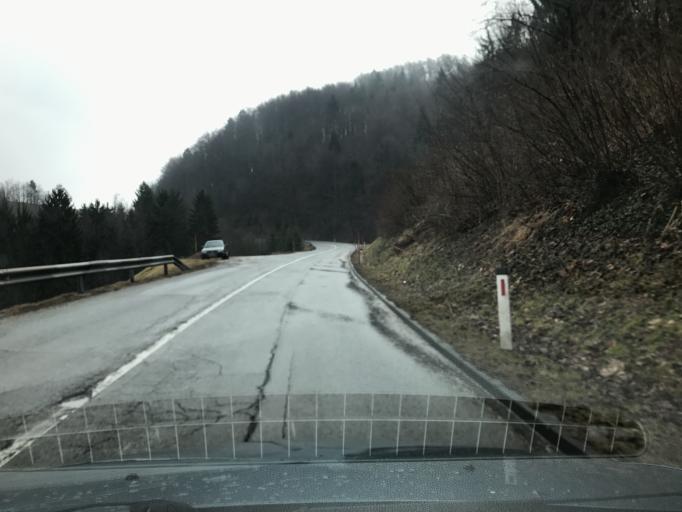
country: SI
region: Gornji Grad
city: Gornji Grad
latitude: 46.2156
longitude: 14.7998
